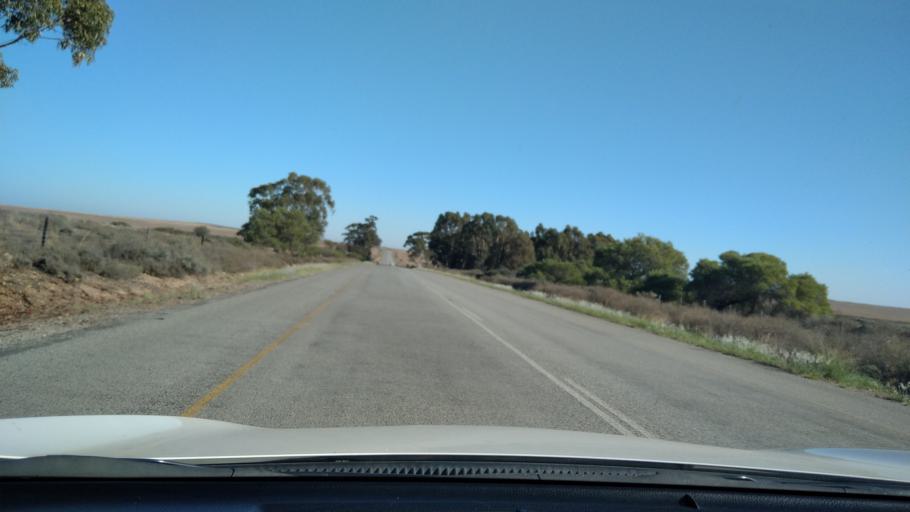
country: ZA
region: Western Cape
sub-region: West Coast District Municipality
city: Moorreesburg
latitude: -33.2486
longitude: 18.5800
